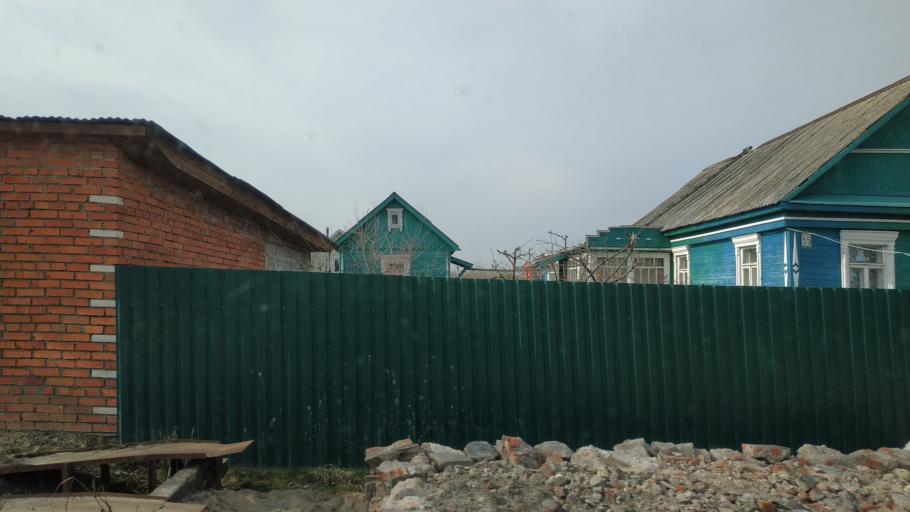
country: RU
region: Moskovskaya
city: Beloozerskiy
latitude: 55.4345
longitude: 38.4883
